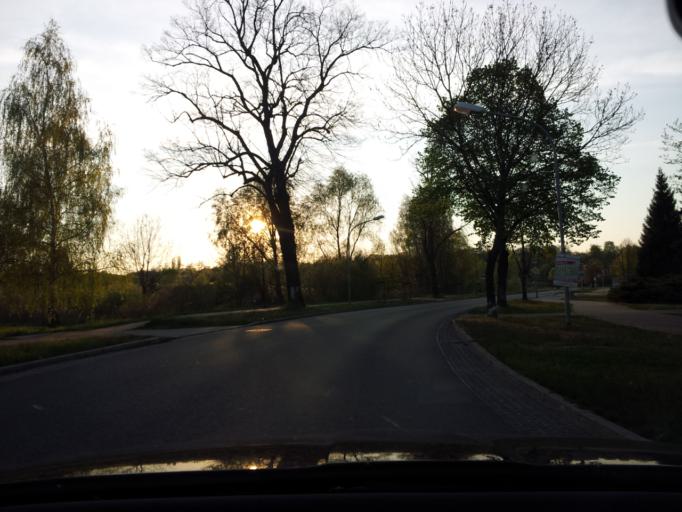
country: DE
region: Brandenburg
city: Juterbog
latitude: 51.9942
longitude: 13.0584
